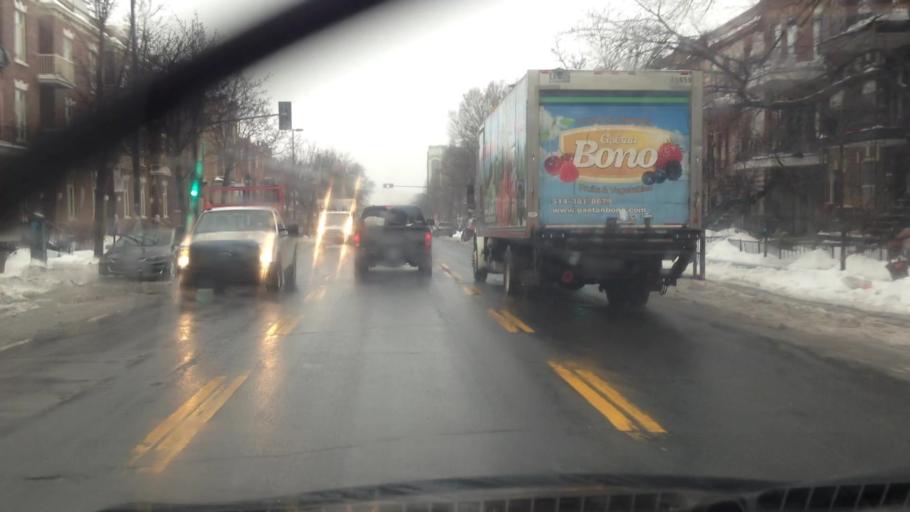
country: CA
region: Quebec
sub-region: Montreal
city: Montreal
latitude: 45.5244
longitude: -73.6070
